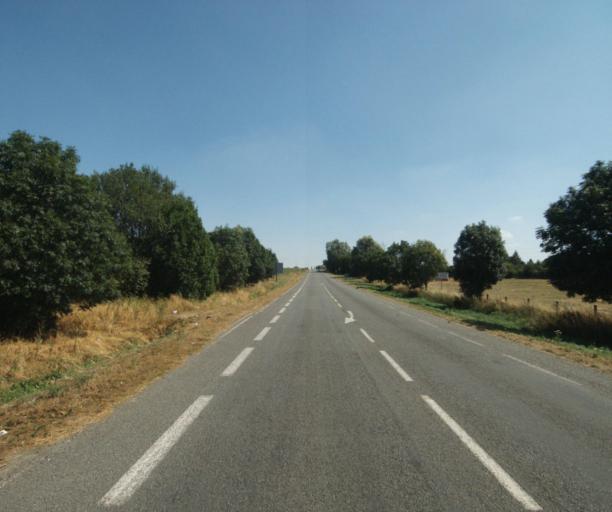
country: FR
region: Nord-Pas-de-Calais
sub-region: Departement du Nord
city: Bousbecque
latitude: 50.7726
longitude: 3.0996
